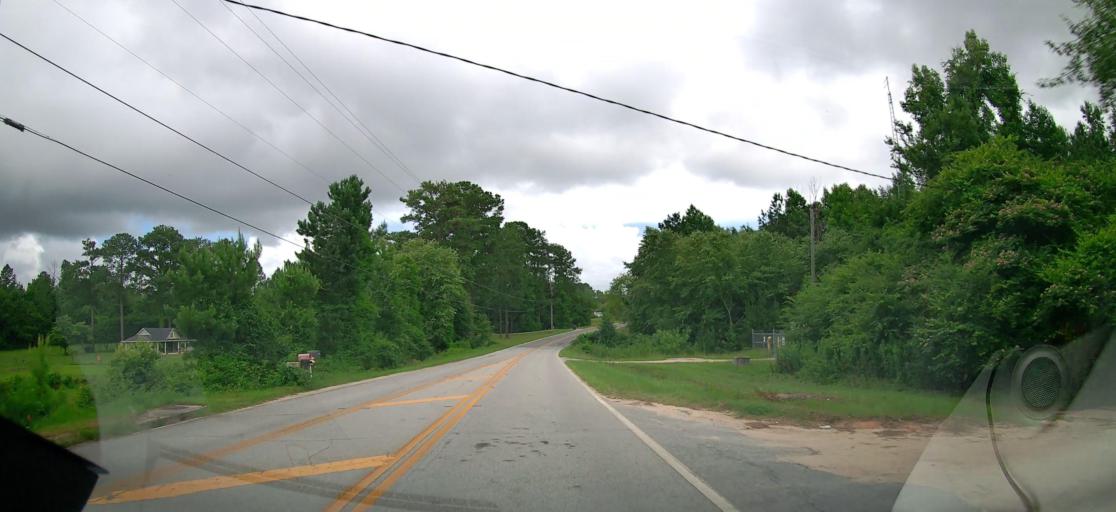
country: US
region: Georgia
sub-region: Bibb County
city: West Point
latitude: 32.7509
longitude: -83.7644
